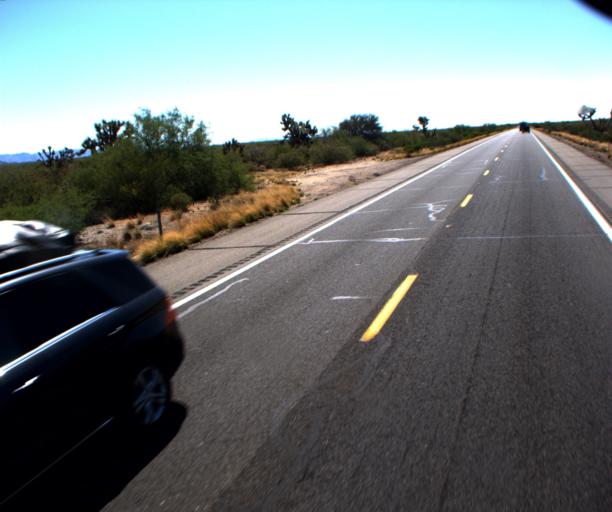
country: US
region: Arizona
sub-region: Yavapai County
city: Congress
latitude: 34.1664
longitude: -113.0125
